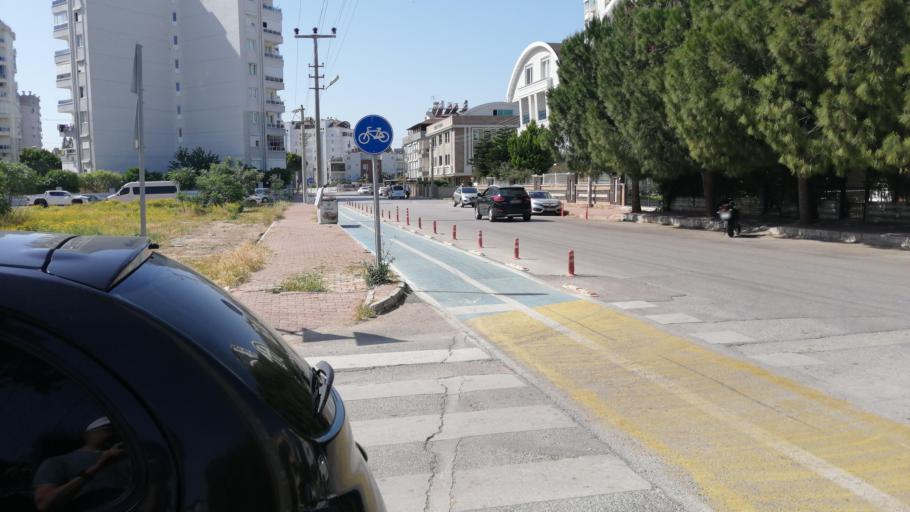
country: TR
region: Antalya
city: Antalya
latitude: 36.8581
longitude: 30.7834
